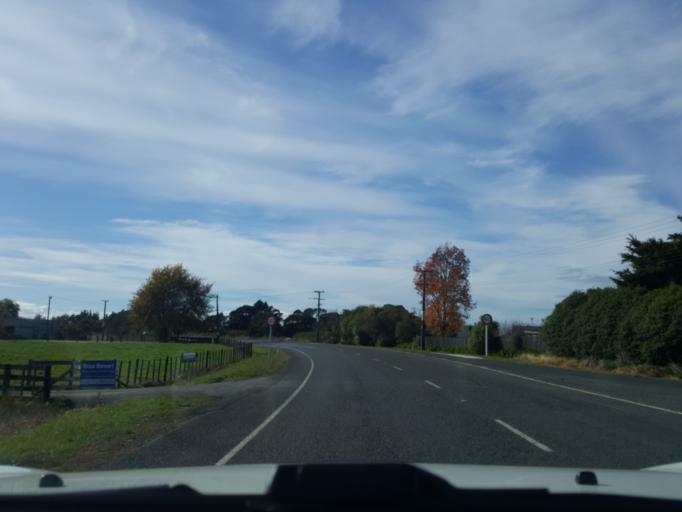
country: NZ
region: Waikato
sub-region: Waikato District
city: Ngaruawahia
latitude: -37.6096
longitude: 175.1953
